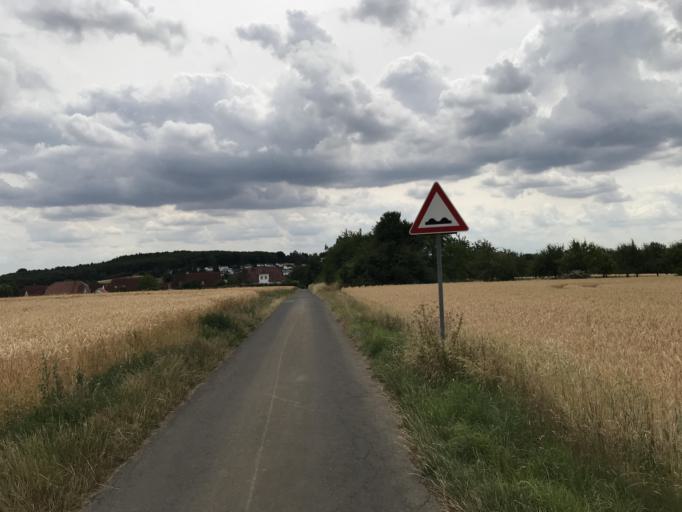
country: DE
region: Hesse
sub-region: Regierungsbezirk Giessen
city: Grunberg
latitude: 50.5799
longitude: 8.9343
